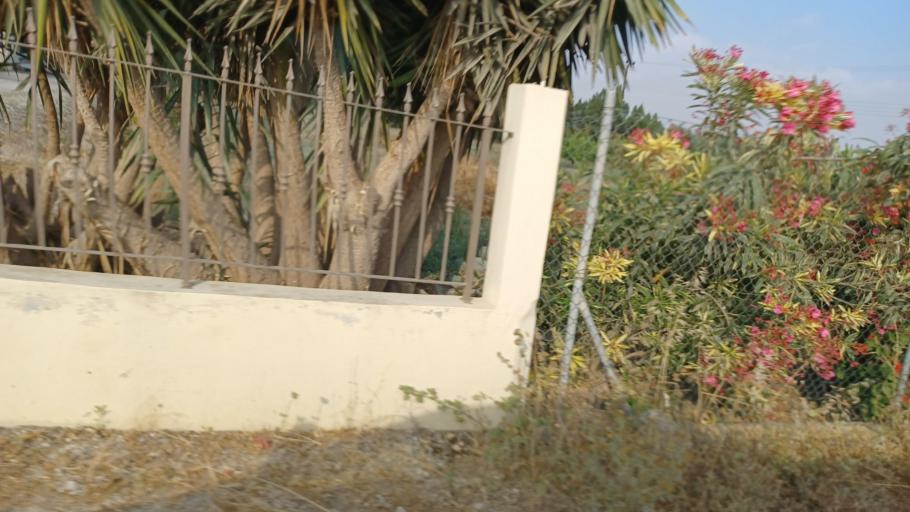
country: CY
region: Larnaka
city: Tersefanou
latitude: 34.8275
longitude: 33.5535
